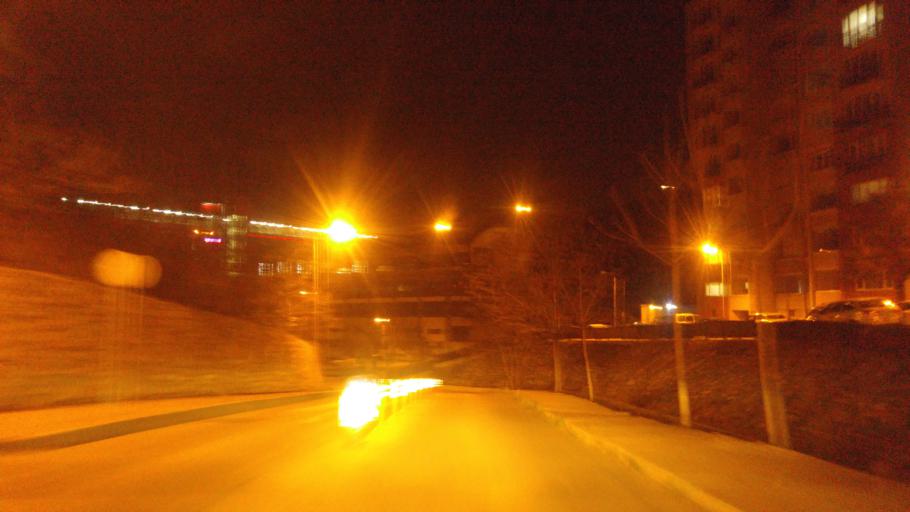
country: TR
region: Karabuk
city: Karabuk
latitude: 41.2006
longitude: 32.6153
